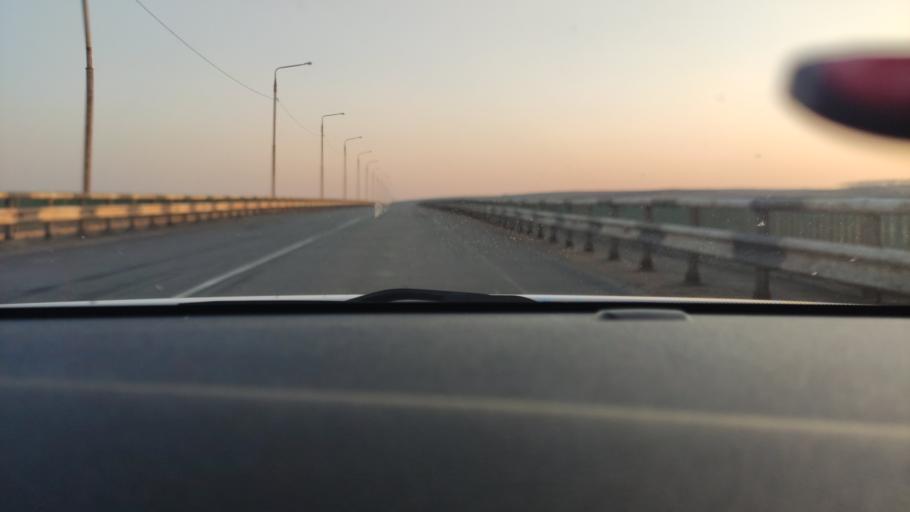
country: RU
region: Voronezj
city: Kolodeznyy
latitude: 51.3381
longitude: 39.1685
